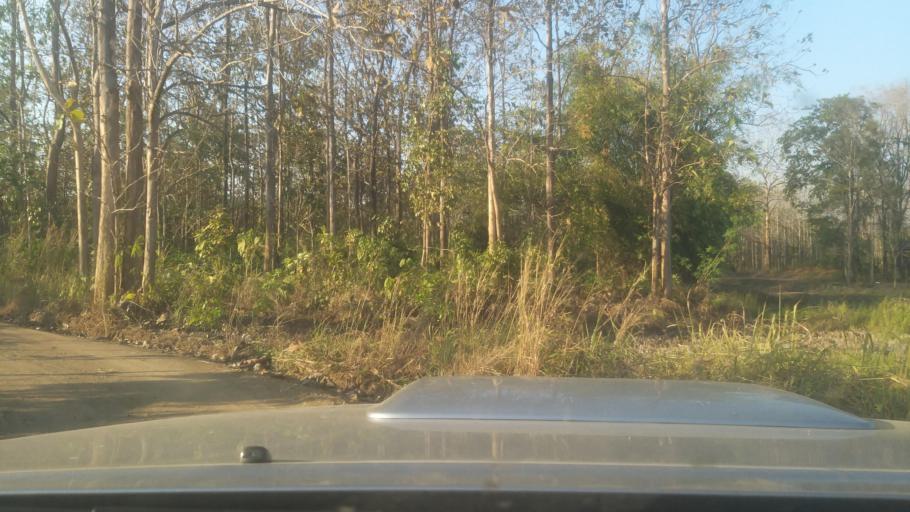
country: TH
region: Phrae
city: Nong Muang Khai
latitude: 18.2743
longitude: 100.0259
